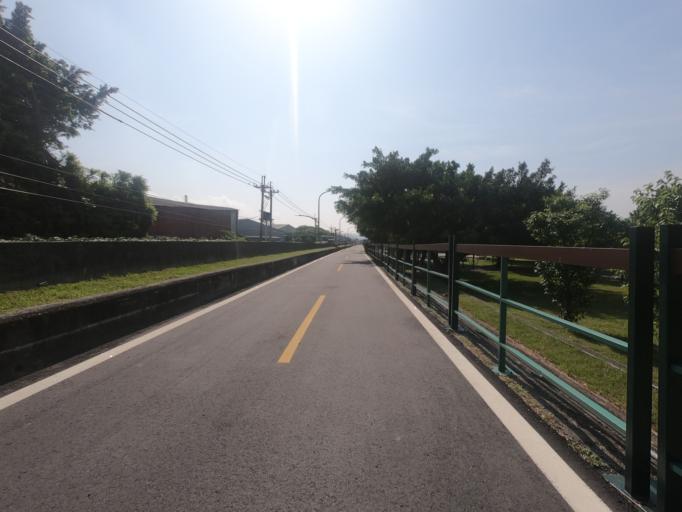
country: TW
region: Taipei
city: Taipei
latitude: 25.1054
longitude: 121.4756
